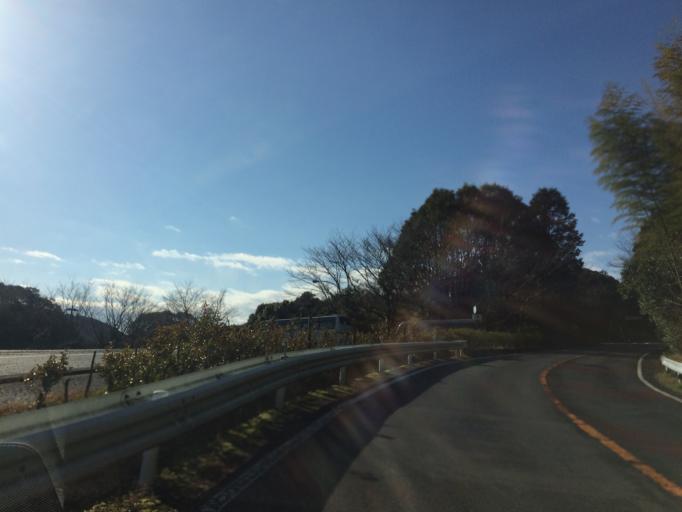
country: JP
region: Shizuoka
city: Shizuoka-shi
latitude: 34.9794
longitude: 138.4476
